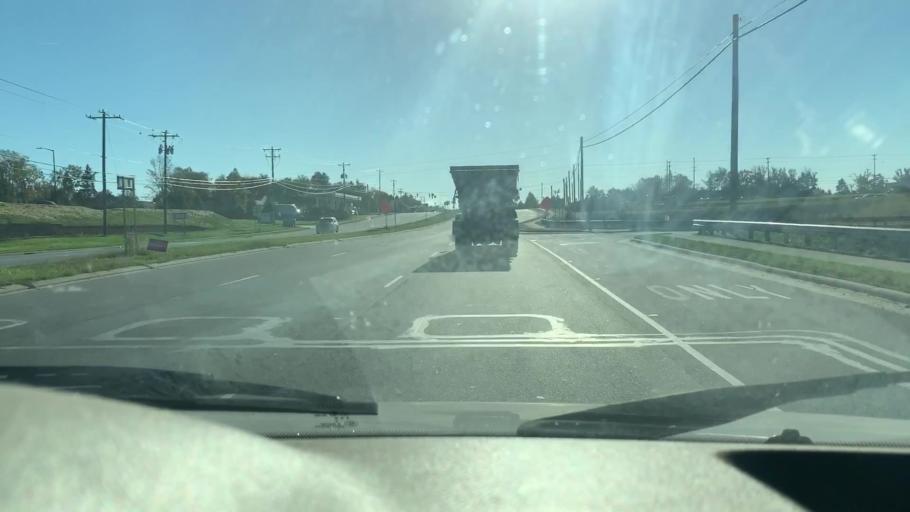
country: US
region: North Carolina
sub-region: Cabarrus County
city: Harrisburg
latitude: 35.4085
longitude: -80.7161
